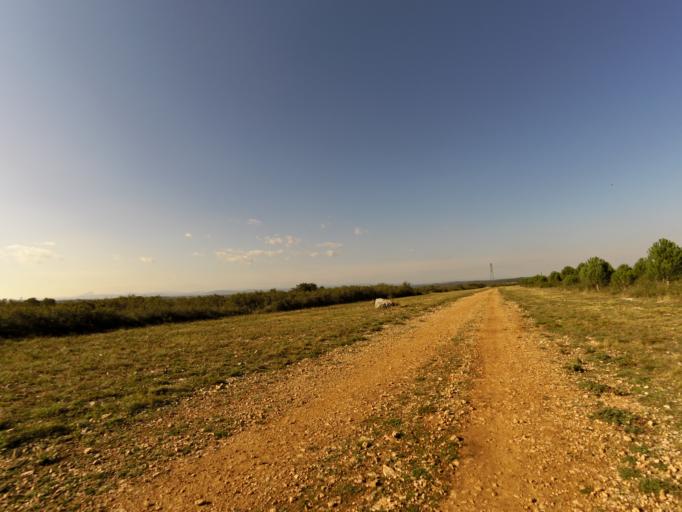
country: FR
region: Languedoc-Roussillon
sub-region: Departement de l'Herault
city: Villetelle
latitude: 43.7292
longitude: 4.1278
